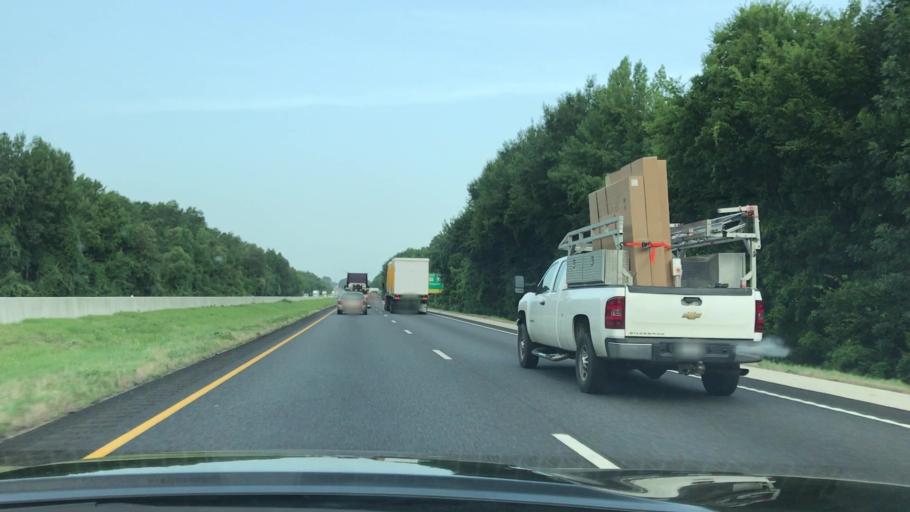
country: US
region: Texas
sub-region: Gregg County
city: Kilgore
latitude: 32.4352
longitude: -94.8086
